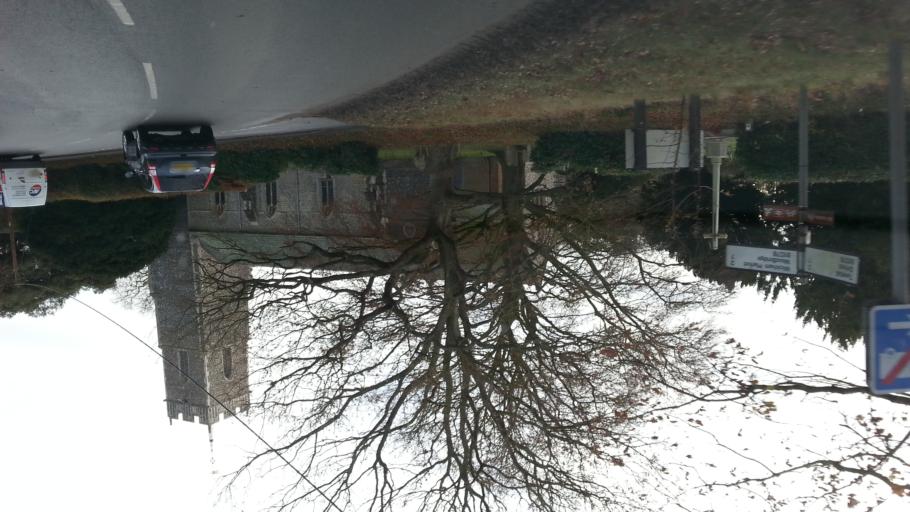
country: GB
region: England
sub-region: Suffolk
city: Wickham Market
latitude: 52.1527
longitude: 1.4049
